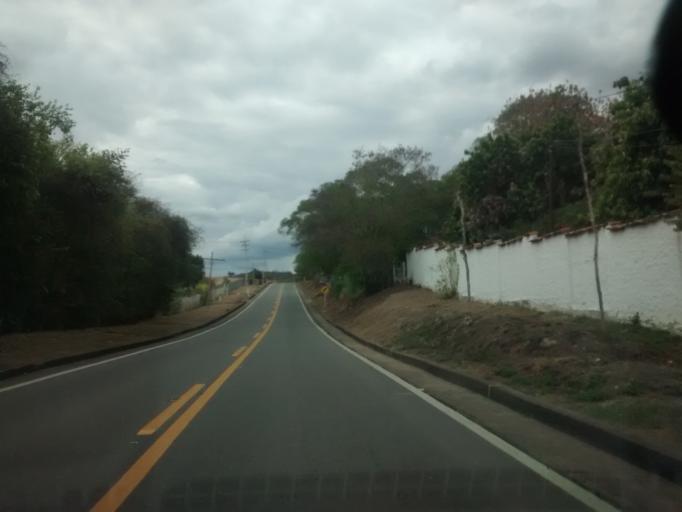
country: CO
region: Cundinamarca
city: Agua de Dios
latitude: 4.4230
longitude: -74.7026
